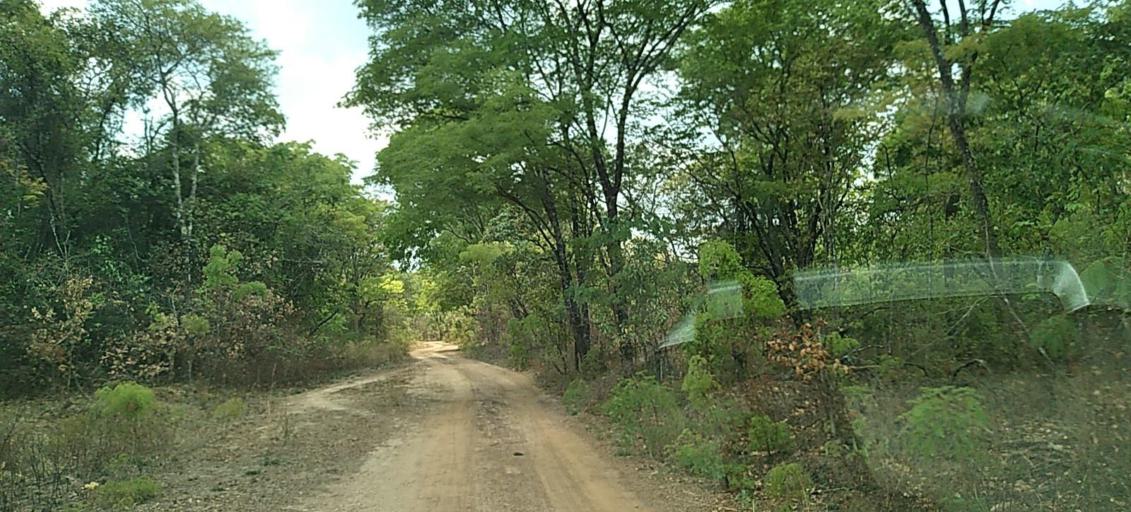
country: ZM
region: Copperbelt
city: Chingola
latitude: -12.7688
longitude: 27.7028
